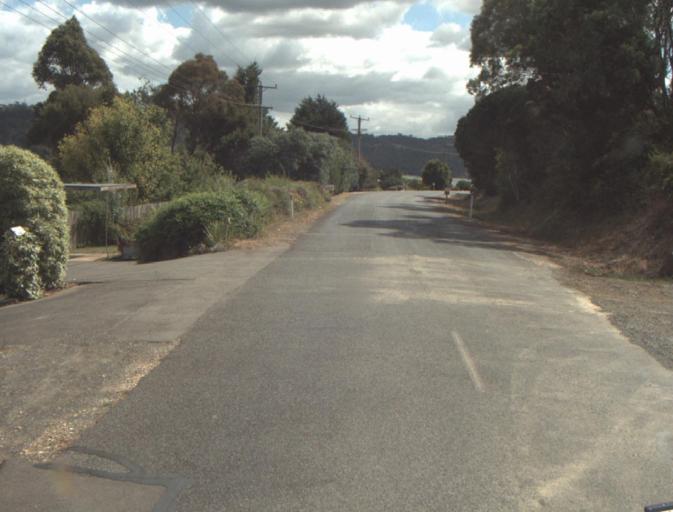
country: AU
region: Tasmania
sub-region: Launceston
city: Mayfield
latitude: -41.3150
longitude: 147.0191
